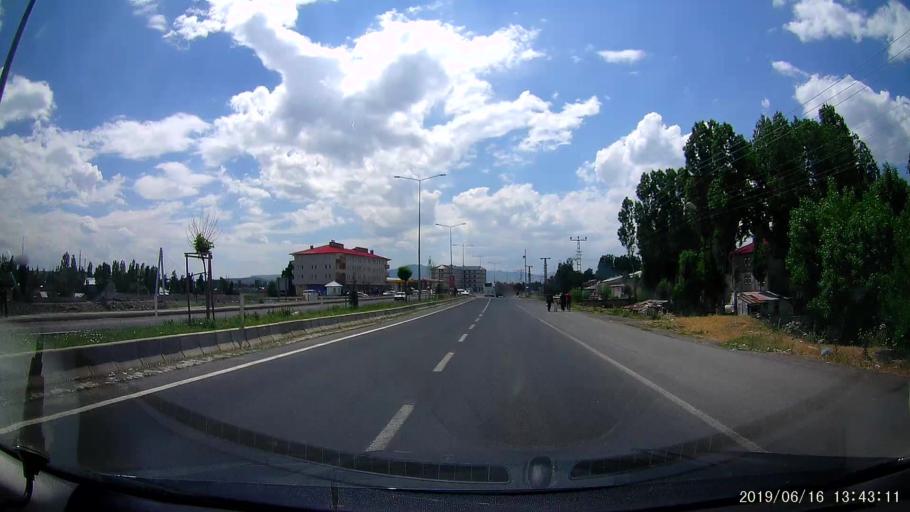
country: TR
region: Agri
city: Agri
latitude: 39.7085
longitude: 43.0587
